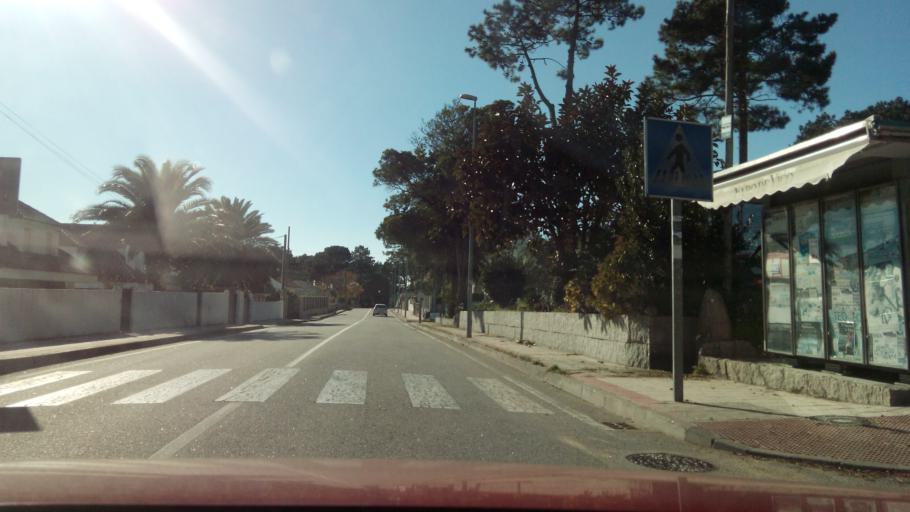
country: ES
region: Galicia
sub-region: Provincia de Pontevedra
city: O Grove
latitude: 42.4578
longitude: -8.9224
